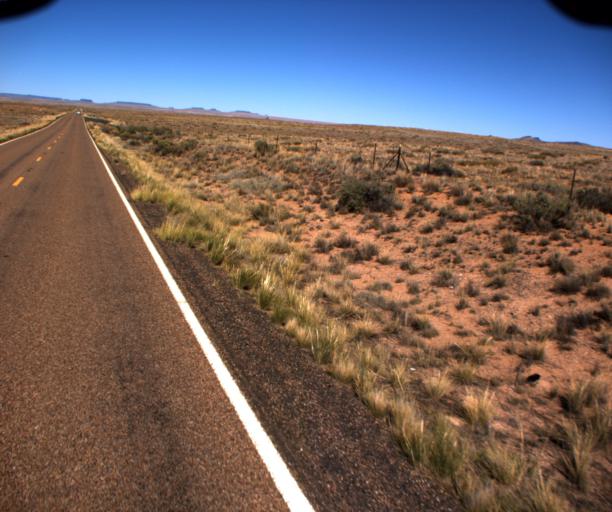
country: US
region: Arizona
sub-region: Navajo County
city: Holbrook
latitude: 35.0110
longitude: -110.0899
